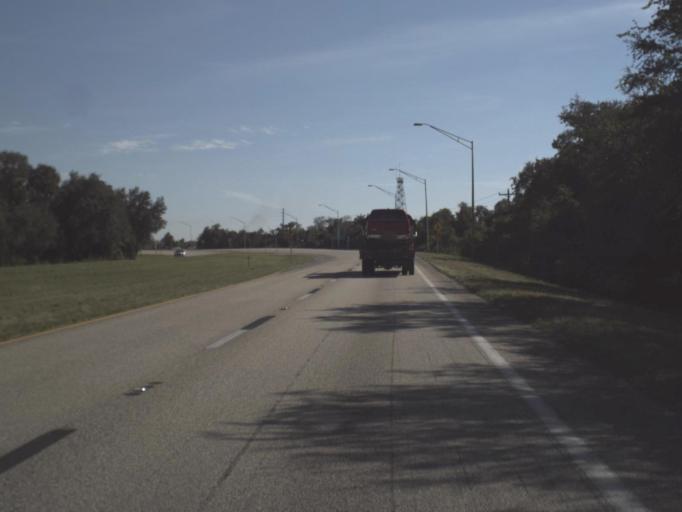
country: US
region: Florida
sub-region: Hendry County
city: Port LaBelle
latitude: 26.9289
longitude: -81.3143
